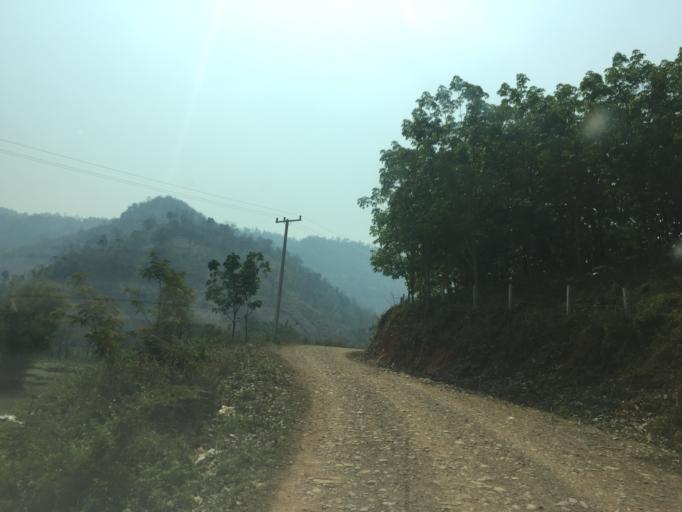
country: TH
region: Phayao
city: Phu Sang
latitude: 19.5721
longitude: 100.5253
